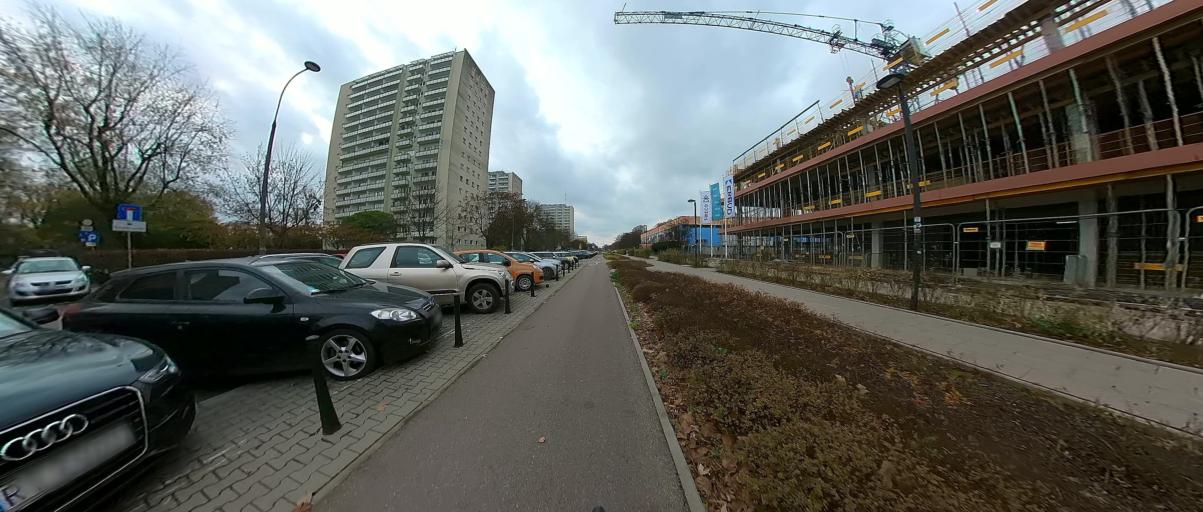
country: PL
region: Masovian Voivodeship
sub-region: Warszawa
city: Warsaw
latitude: 52.2118
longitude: 21.0109
